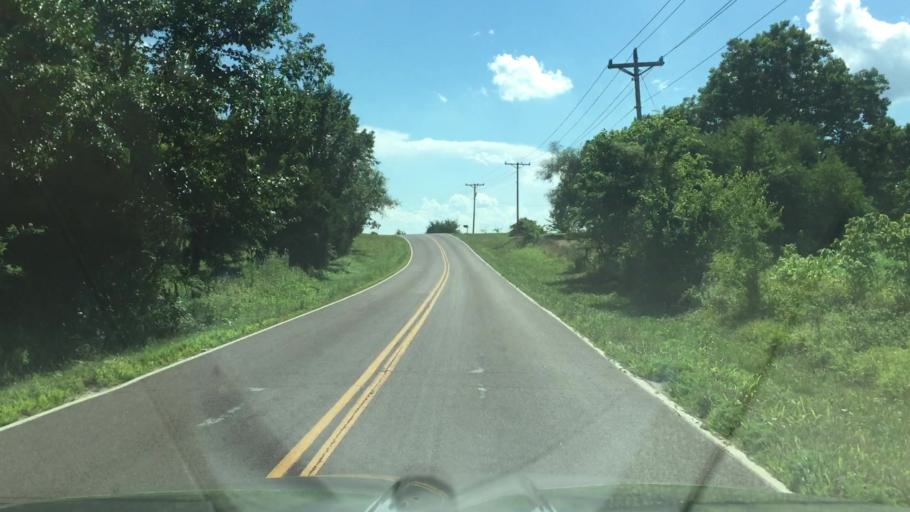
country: US
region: Missouri
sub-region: Miller County
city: Tuscumbia
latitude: 38.1248
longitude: -92.4650
